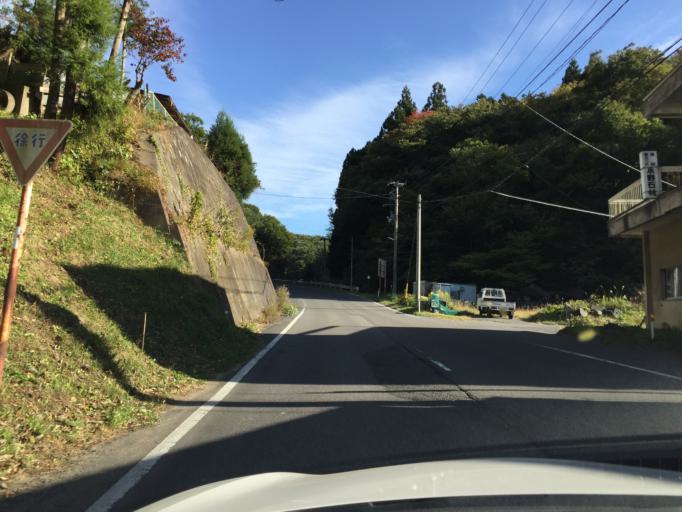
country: JP
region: Fukushima
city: Miharu
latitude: 37.3601
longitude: 140.5313
